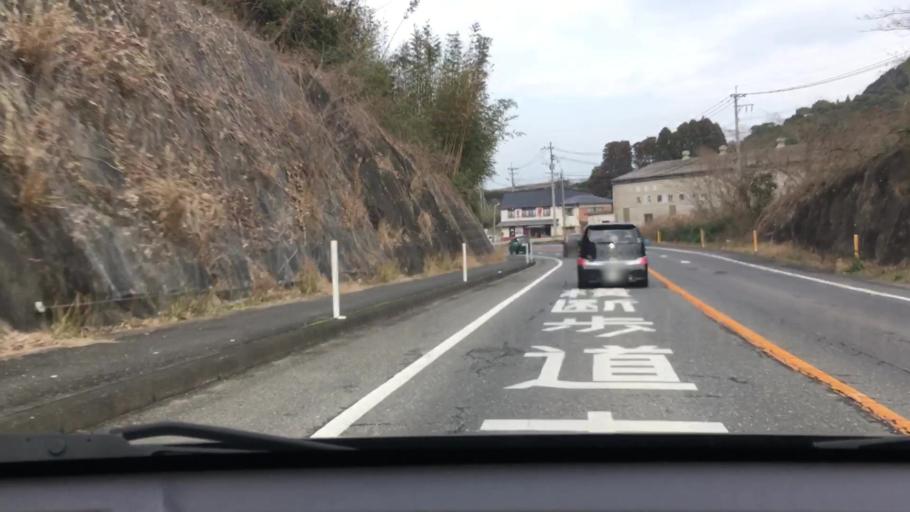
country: JP
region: Saga Prefecture
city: Imaricho-ko
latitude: 33.3211
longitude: 129.9288
